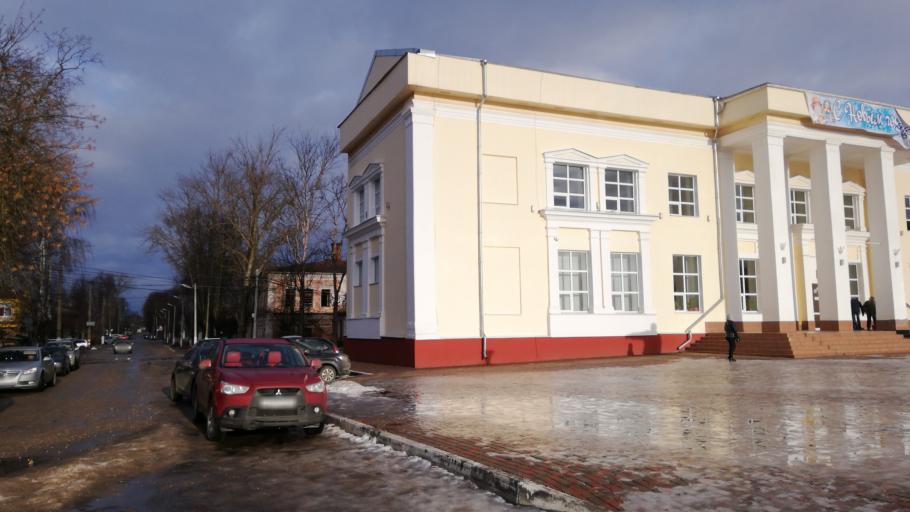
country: RU
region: Jaroslavl
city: Pereslavl'-Zalesskiy
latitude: 56.7394
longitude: 38.8536
